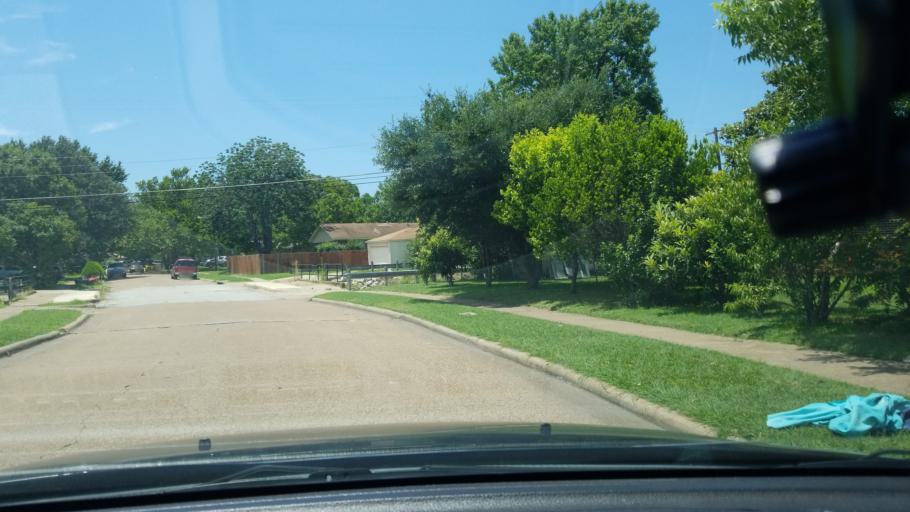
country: US
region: Texas
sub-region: Dallas County
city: Mesquite
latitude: 32.7977
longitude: -96.6554
